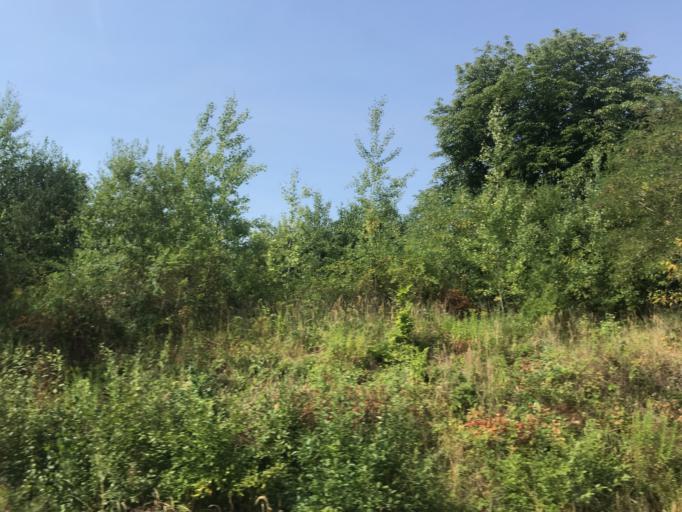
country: CZ
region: Central Bohemia
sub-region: Okres Praha-Vychod
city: Strancice
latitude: 49.9557
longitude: 14.6567
